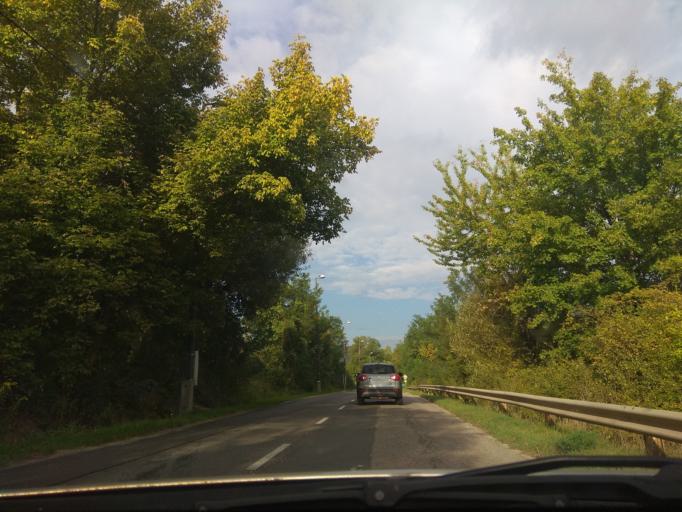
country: HU
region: Borsod-Abauj-Zemplen
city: Miskolc
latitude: 48.0873
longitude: 20.7203
